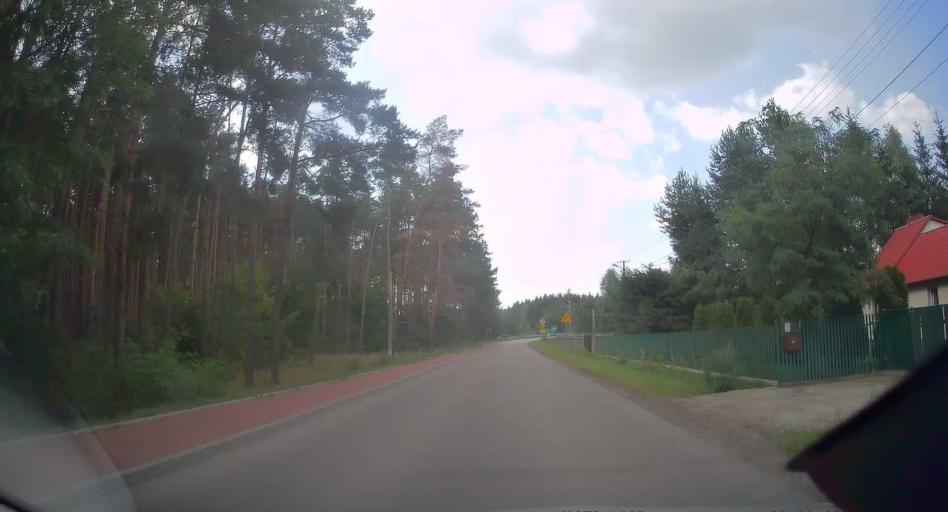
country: PL
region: Swietokrzyskie
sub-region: Powiat konecki
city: Ruda Maleniecka
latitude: 51.1216
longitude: 20.2587
